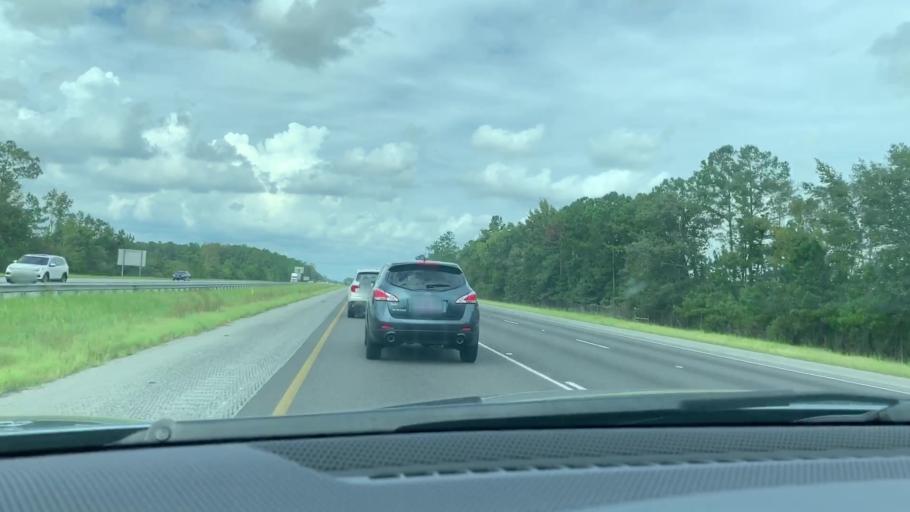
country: US
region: Georgia
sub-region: Liberty County
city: Midway
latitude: 31.6664
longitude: -81.3924
